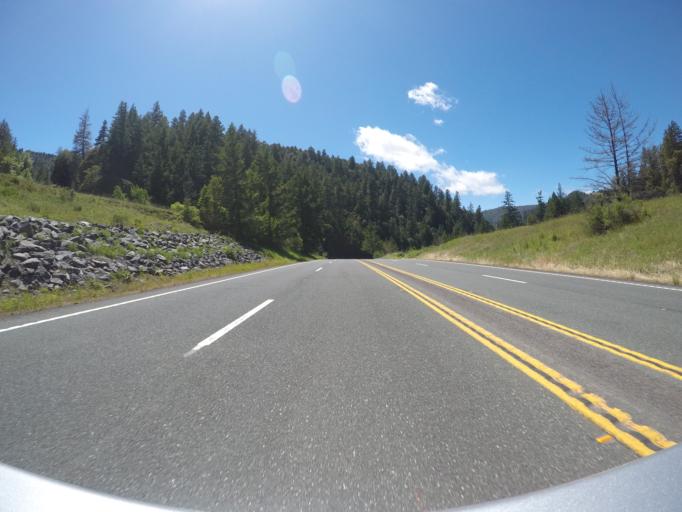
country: US
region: California
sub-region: Mendocino County
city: Laytonville
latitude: 39.8277
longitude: -123.6074
